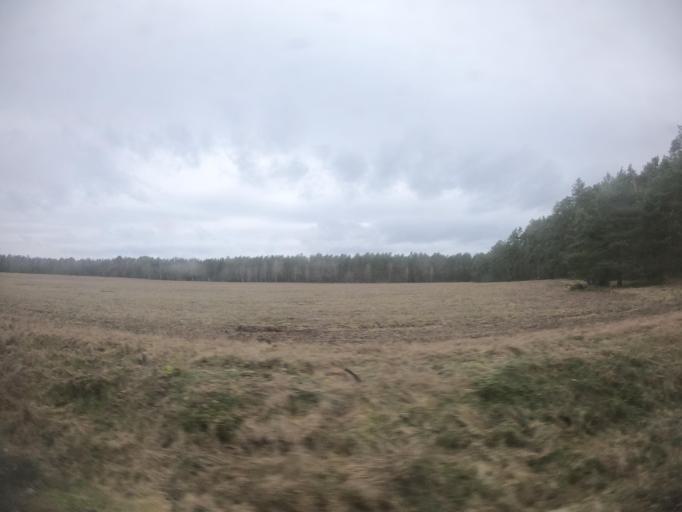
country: PL
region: West Pomeranian Voivodeship
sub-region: Powiat szczecinecki
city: Bialy Bor
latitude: 53.8275
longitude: 16.8722
